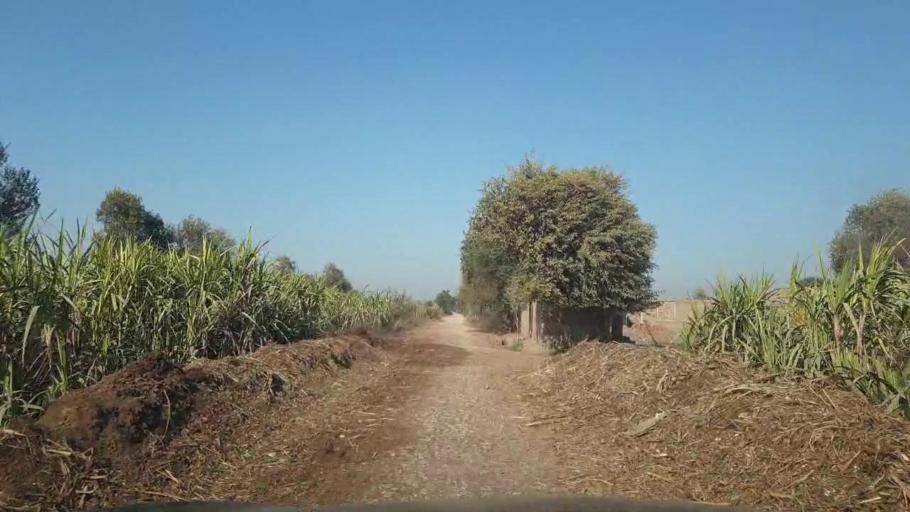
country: PK
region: Sindh
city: Mirpur Mathelo
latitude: 27.9956
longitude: 69.4794
